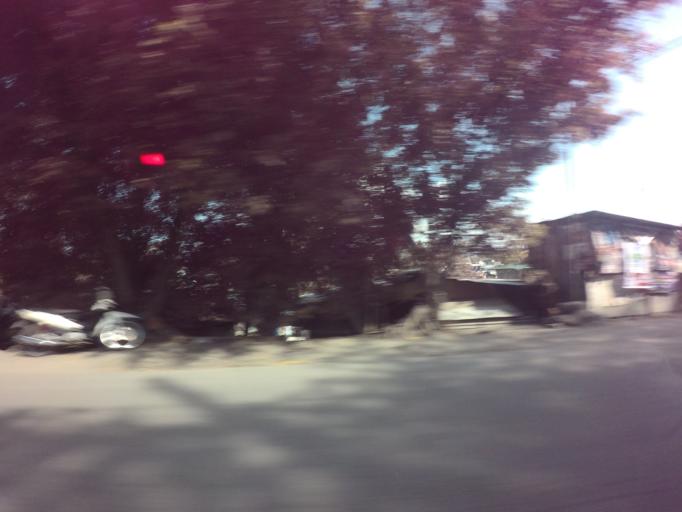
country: PH
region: Calabarzon
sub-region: Province of Rizal
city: Taguig
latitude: 14.5098
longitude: 121.0453
